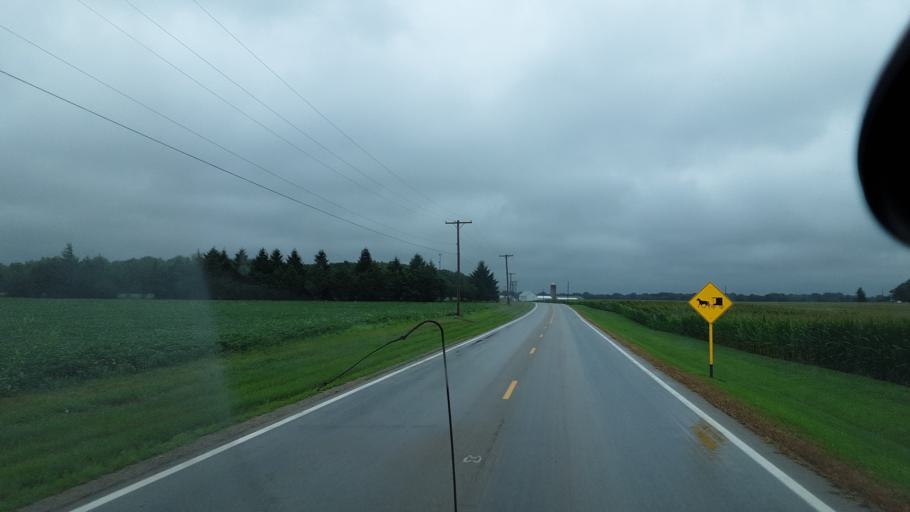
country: US
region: Ohio
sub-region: Mercer County
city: Rockford
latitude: 40.7480
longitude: -84.7722
